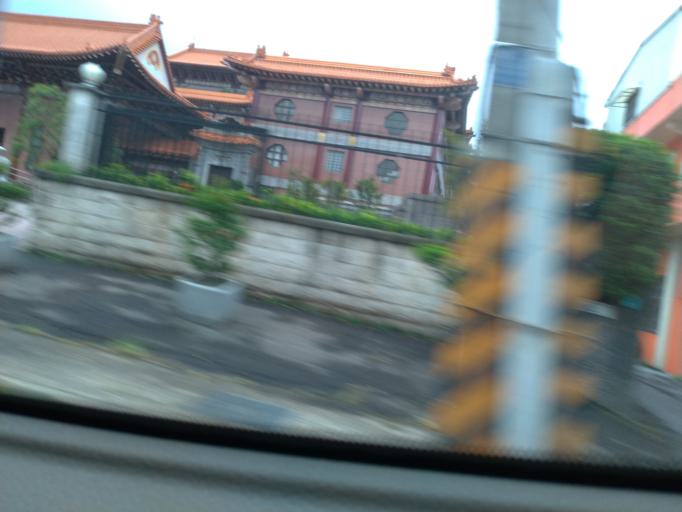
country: TW
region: Taipei
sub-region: Taipei
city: Banqiao
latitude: 24.9312
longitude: 121.4091
